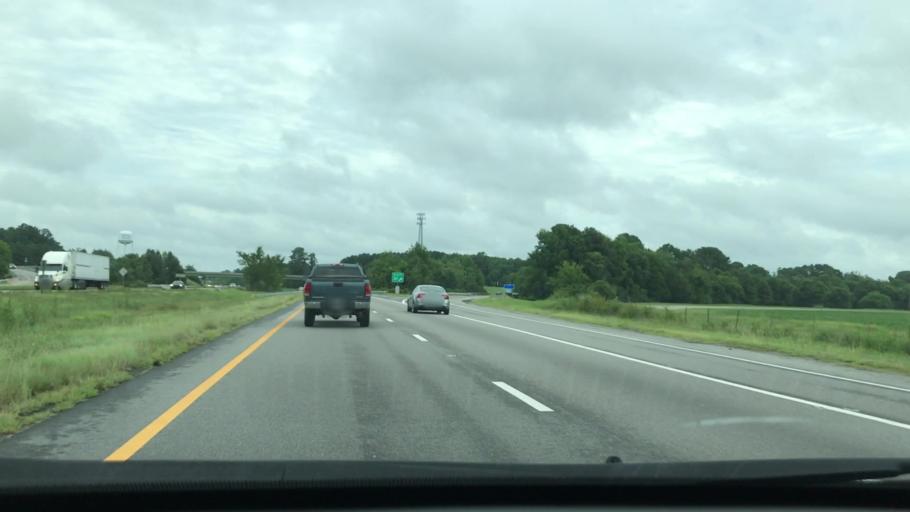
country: US
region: Virginia
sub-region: Sussex County
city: Sussex
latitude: 36.9396
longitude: -77.3928
